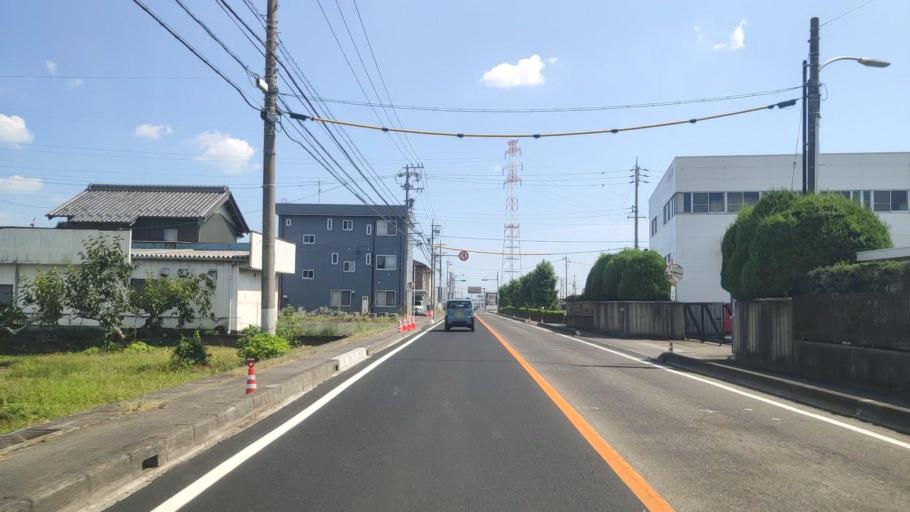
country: JP
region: Gifu
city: Godo
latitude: 35.4641
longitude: 136.6758
